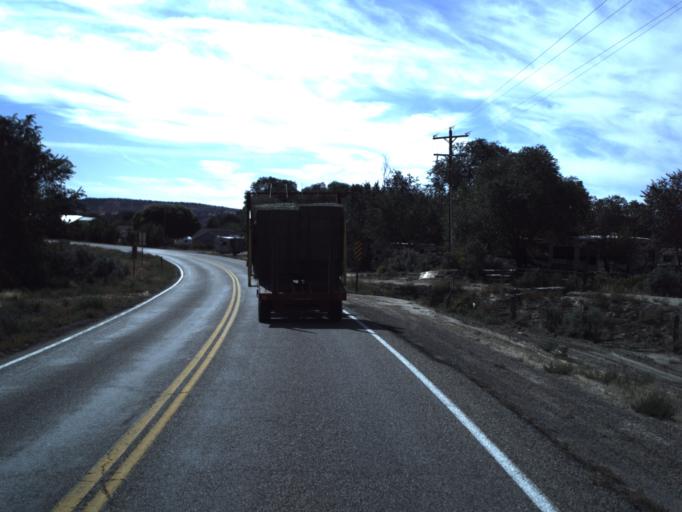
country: US
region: Utah
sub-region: Garfield County
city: Panguitch
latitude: 37.5714
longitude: -112.0568
